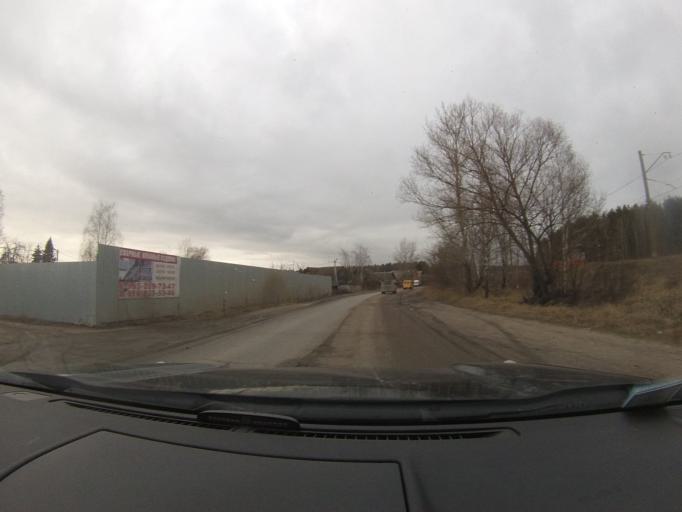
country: RU
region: Moskovskaya
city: Voskresensk
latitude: 55.3300
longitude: 38.6794
